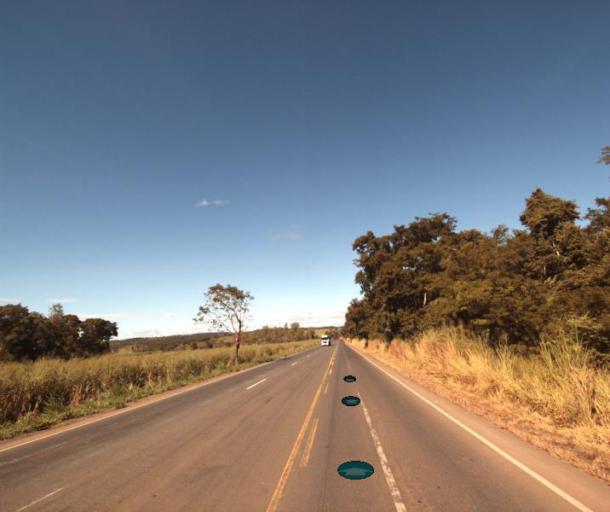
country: BR
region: Goias
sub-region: Itapaci
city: Itapaci
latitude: -14.9927
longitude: -49.4060
